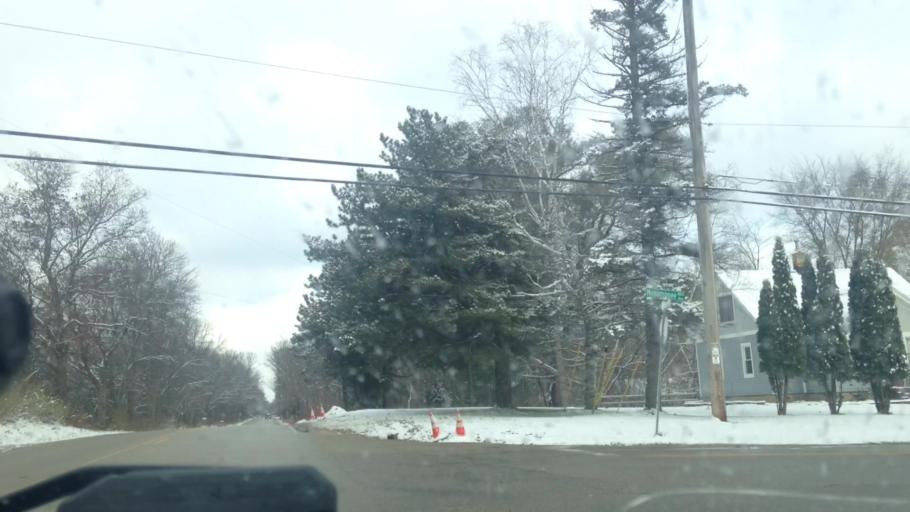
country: US
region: Wisconsin
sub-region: Waukesha County
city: Lannon
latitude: 43.1698
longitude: -88.1831
